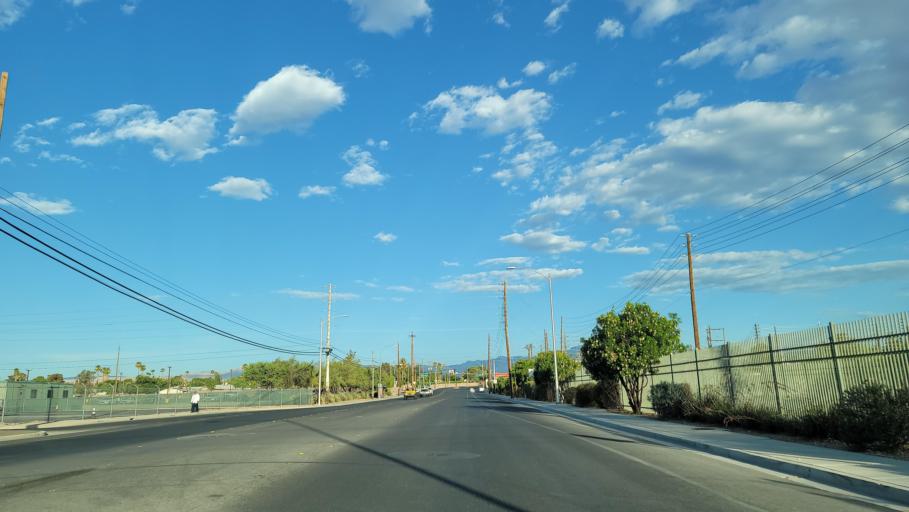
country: US
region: Nevada
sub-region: Clark County
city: Las Vegas
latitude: 36.1663
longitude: -115.1897
